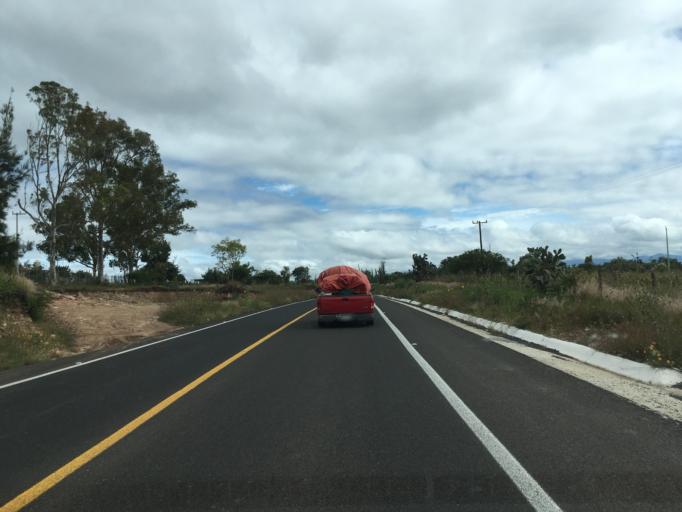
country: MX
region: Hidalgo
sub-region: Atotonilco el Grande
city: Santa Maria Amajac
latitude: 20.4065
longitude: -98.7109
